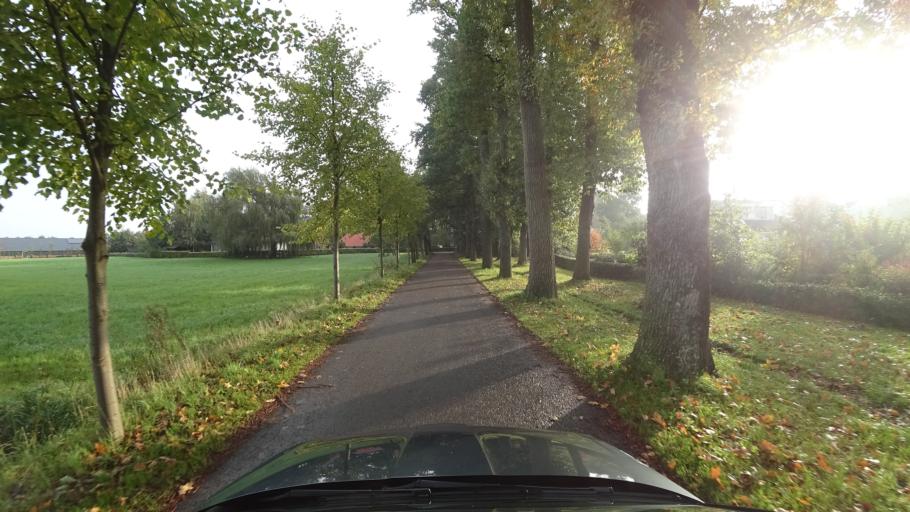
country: NL
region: Gelderland
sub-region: Gemeente Ede
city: Ede
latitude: 52.0007
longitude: 5.6307
